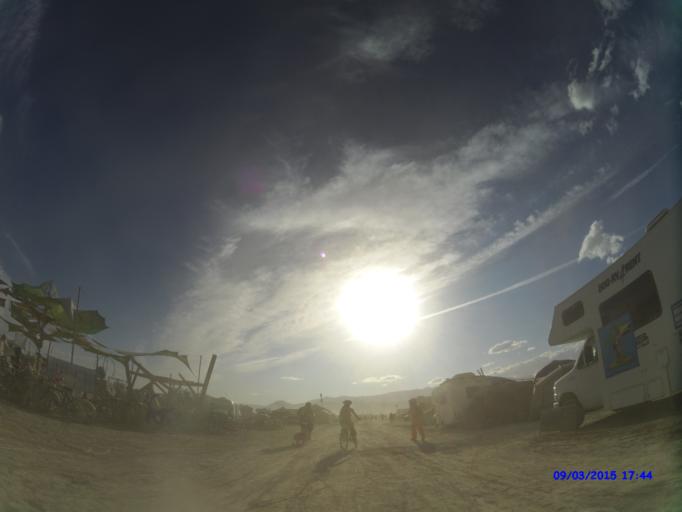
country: US
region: Nevada
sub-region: Pershing County
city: Lovelock
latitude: 40.7753
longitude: -119.2032
